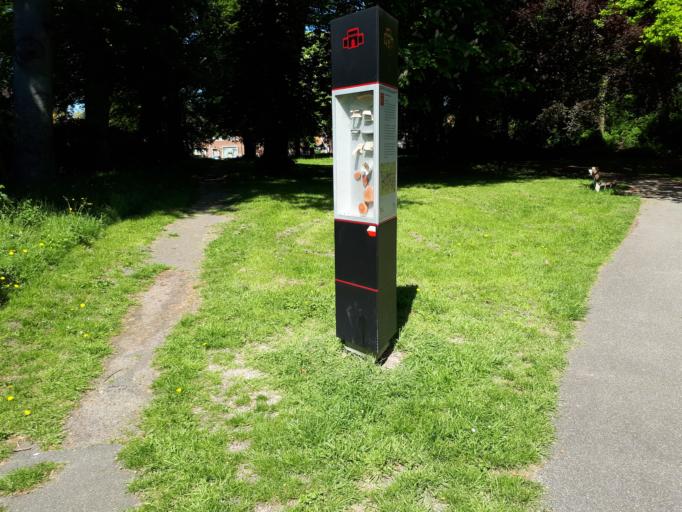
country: NL
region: South Holland
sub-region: Gemeente Leidschendam-Voorburg
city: Voorburg
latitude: 52.0600
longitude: 4.3483
